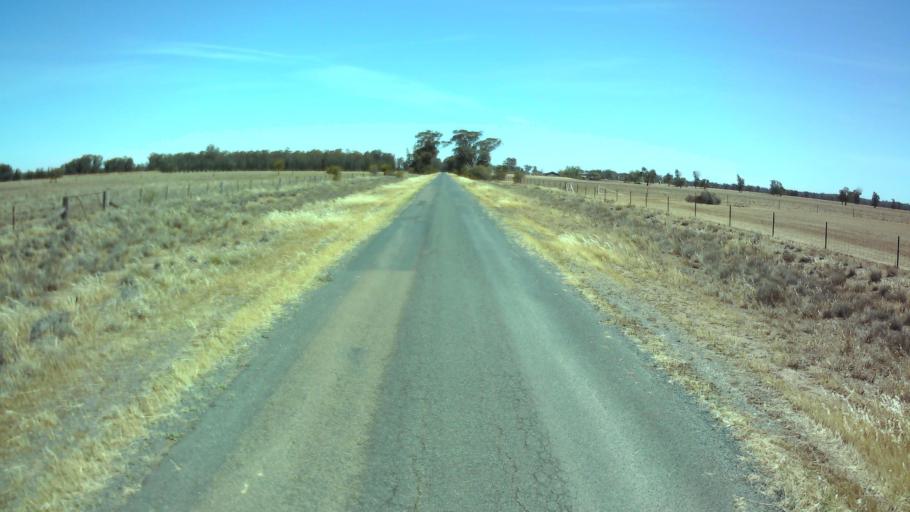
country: AU
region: New South Wales
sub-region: Weddin
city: Grenfell
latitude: -33.8978
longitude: 147.6869
